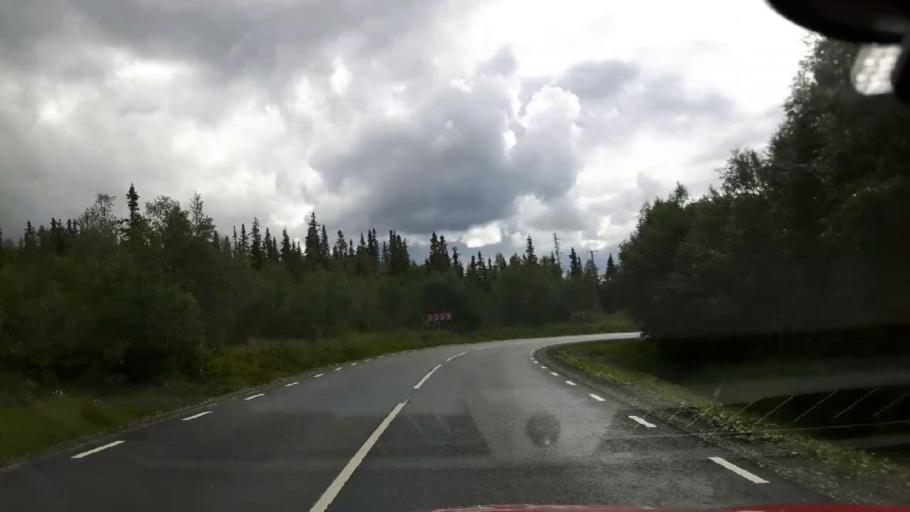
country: NO
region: Nord-Trondelag
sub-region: Royrvik
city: Royrvik
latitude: 64.8789
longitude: 14.2139
